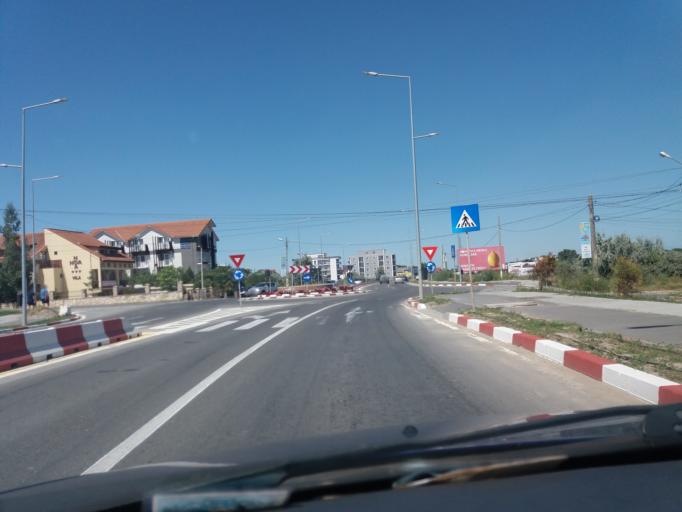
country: RO
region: Constanta
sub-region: Comuna Navodari
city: Navodari
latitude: 44.3065
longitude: 28.6212
